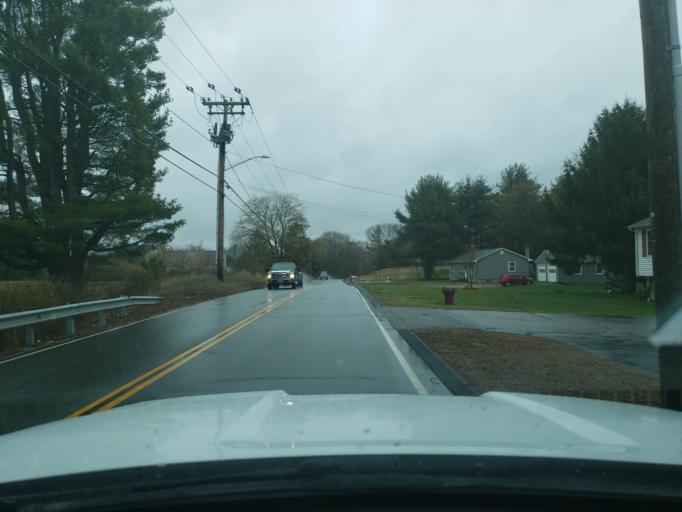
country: US
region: Connecticut
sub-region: Windham County
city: Plainfield Village
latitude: 41.6862
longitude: -71.9347
